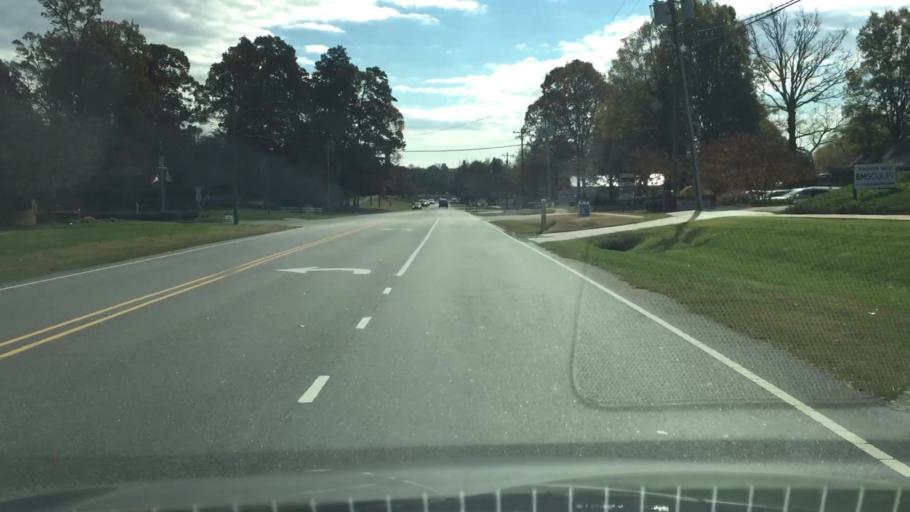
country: US
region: North Carolina
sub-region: Iredell County
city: Mooresville
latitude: 35.5723
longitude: -80.8681
